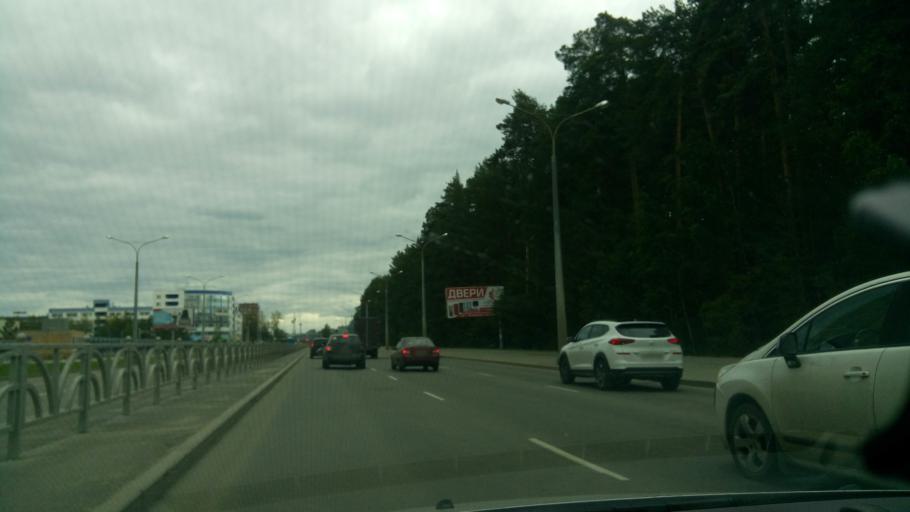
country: RU
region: Sverdlovsk
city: Sovkhoznyy
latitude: 56.7783
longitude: 60.5483
